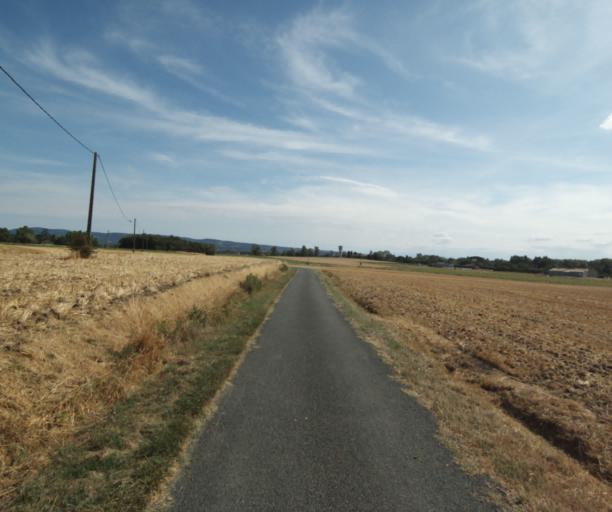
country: FR
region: Midi-Pyrenees
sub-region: Departement de la Haute-Garonne
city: Revel
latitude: 43.5037
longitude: 1.9748
